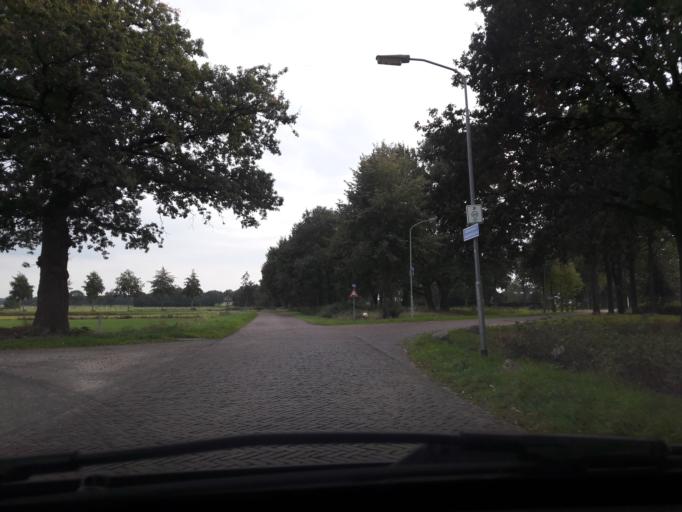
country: NL
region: Drenthe
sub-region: Gemeente Borger-Odoorn
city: Borger
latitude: 52.9519
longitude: 6.8244
